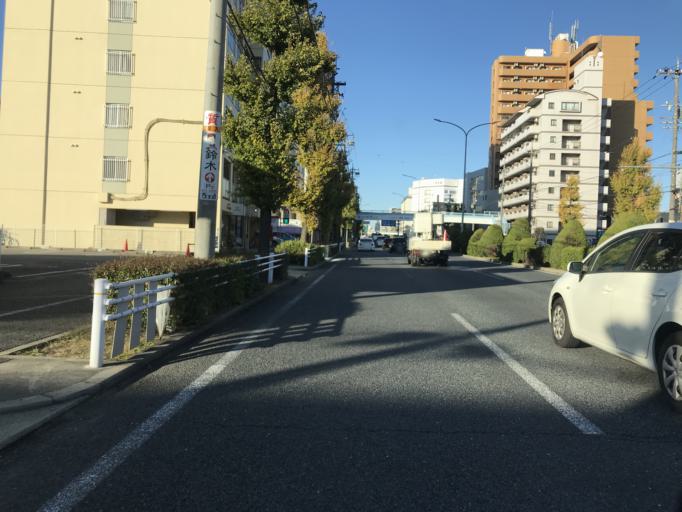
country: JP
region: Aichi
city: Nagoya-shi
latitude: 35.1651
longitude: 136.8718
